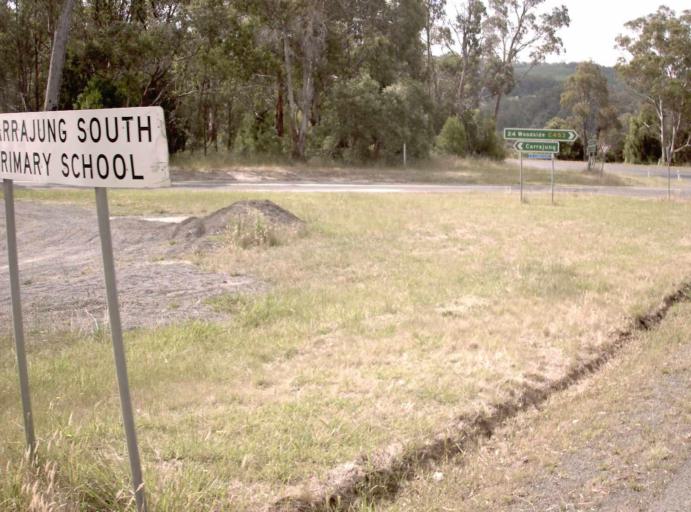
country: AU
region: Victoria
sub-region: Latrobe
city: Traralgon
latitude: -38.3817
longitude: 146.7589
